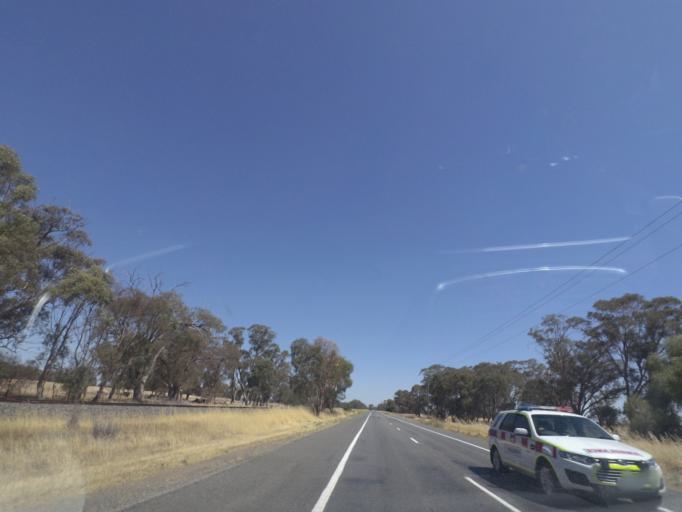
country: AU
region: Victoria
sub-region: Greater Shepparton
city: Shepparton
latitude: -36.2162
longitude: 145.4318
